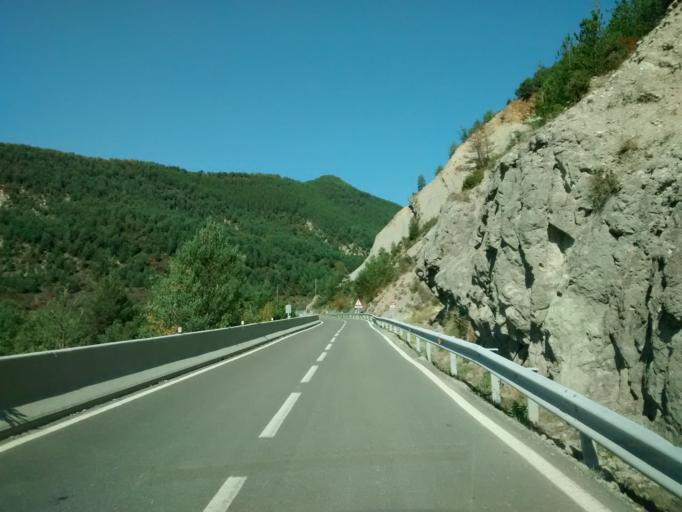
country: ES
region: Aragon
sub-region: Provincia de Huesca
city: Boltana
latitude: 42.4771
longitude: -0.0218
